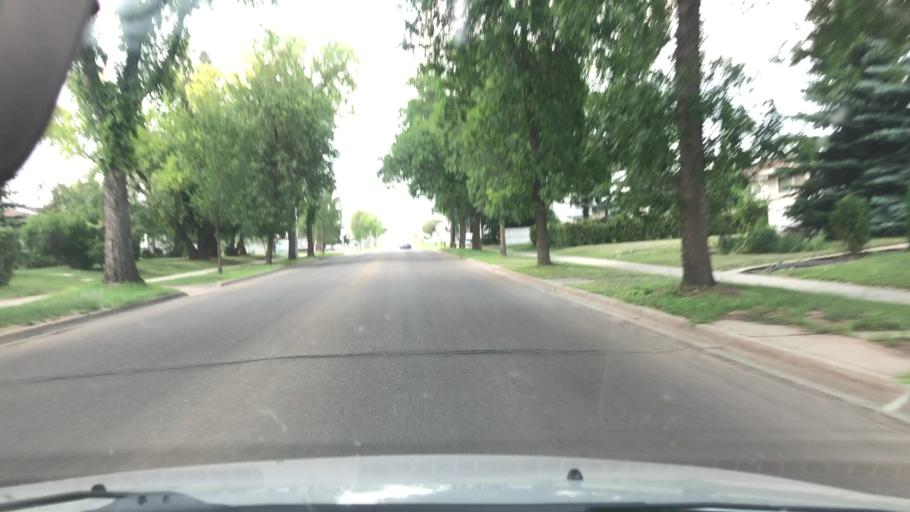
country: CA
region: Alberta
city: Edmonton
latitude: 53.5887
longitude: -113.5165
